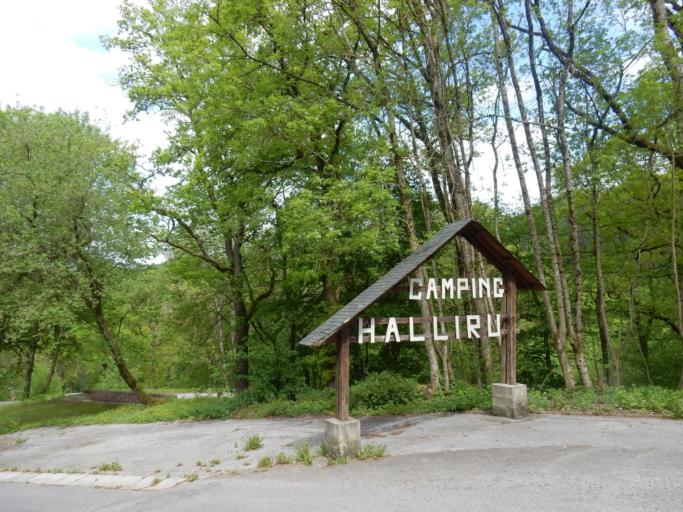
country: BE
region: Wallonia
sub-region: Province du Luxembourg
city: Bouillon
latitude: 49.7900
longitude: 5.0490
